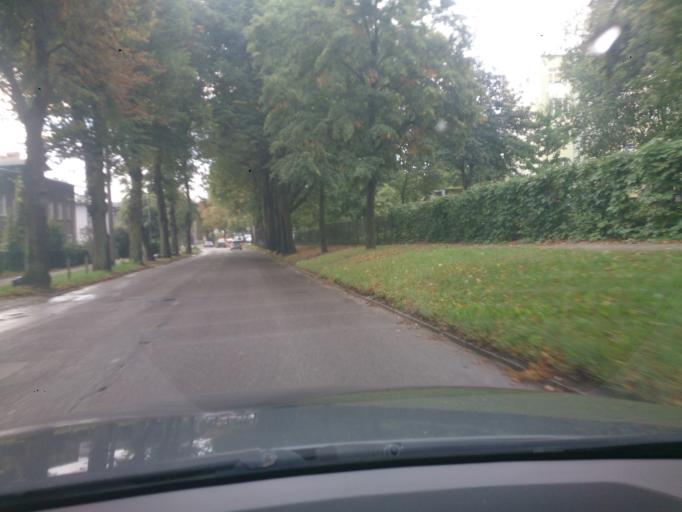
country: PL
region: Pomeranian Voivodeship
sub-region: Sopot
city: Sopot
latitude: 54.3959
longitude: 18.5655
